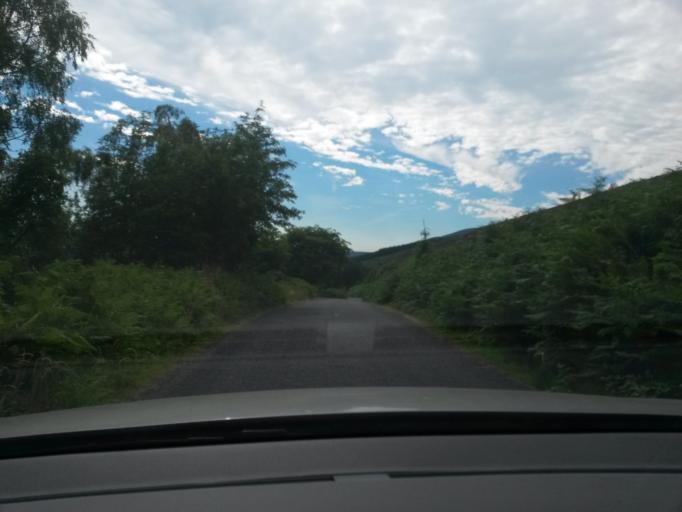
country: IE
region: Leinster
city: Ballinteer
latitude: 53.1841
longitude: -6.2795
